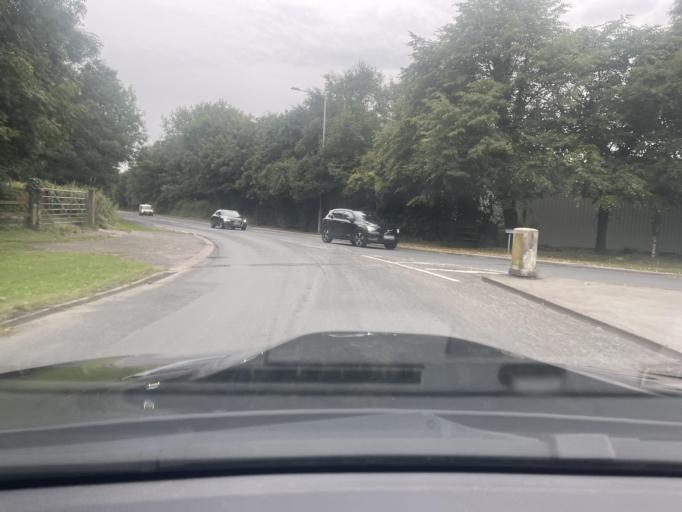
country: GB
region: England
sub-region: Lancashire
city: Leyland
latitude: 53.7006
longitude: -2.7182
